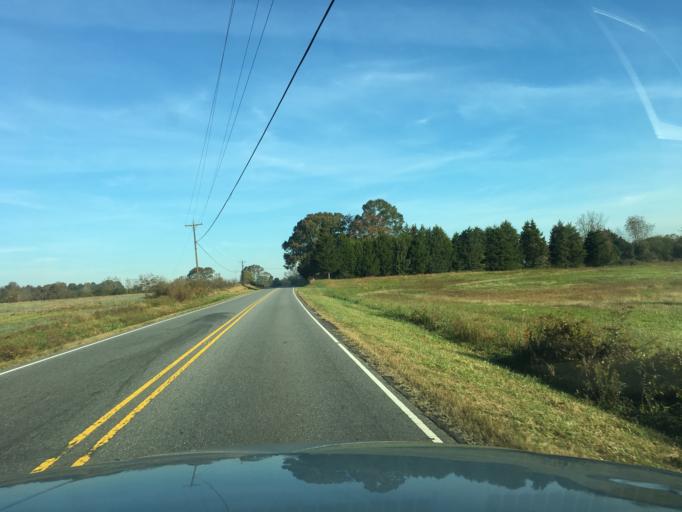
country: US
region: North Carolina
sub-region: Catawba County
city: Maiden
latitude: 35.6160
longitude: -81.2577
